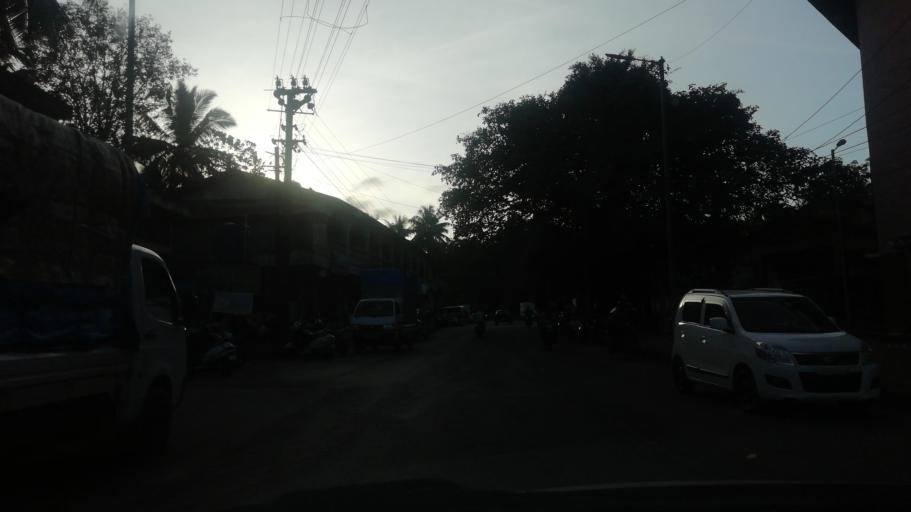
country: IN
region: Goa
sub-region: North Goa
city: Valpoy
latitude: 15.5293
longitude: 74.1350
